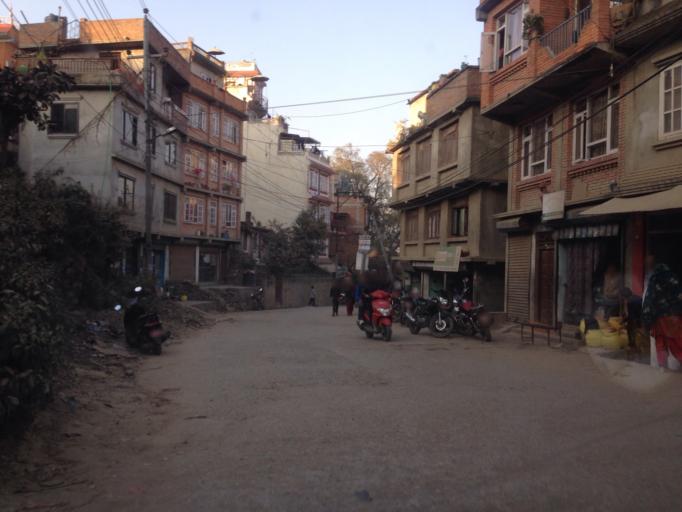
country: NP
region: Central Region
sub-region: Bagmati Zone
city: Kathmandu
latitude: 27.7130
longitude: 85.3008
